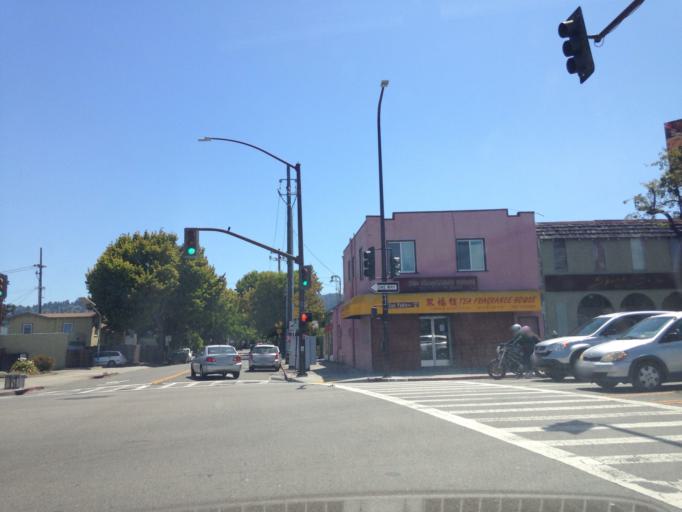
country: US
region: California
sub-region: Alameda County
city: Albany
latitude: 37.8804
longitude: -122.2961
